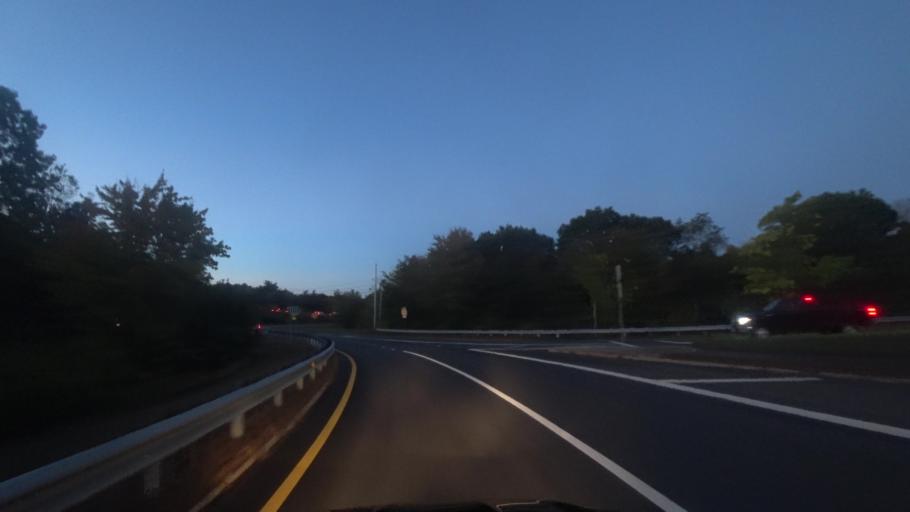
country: US
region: Massachusetts
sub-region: Middlesex County
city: Reading
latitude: 42.5260
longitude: -71.0828
